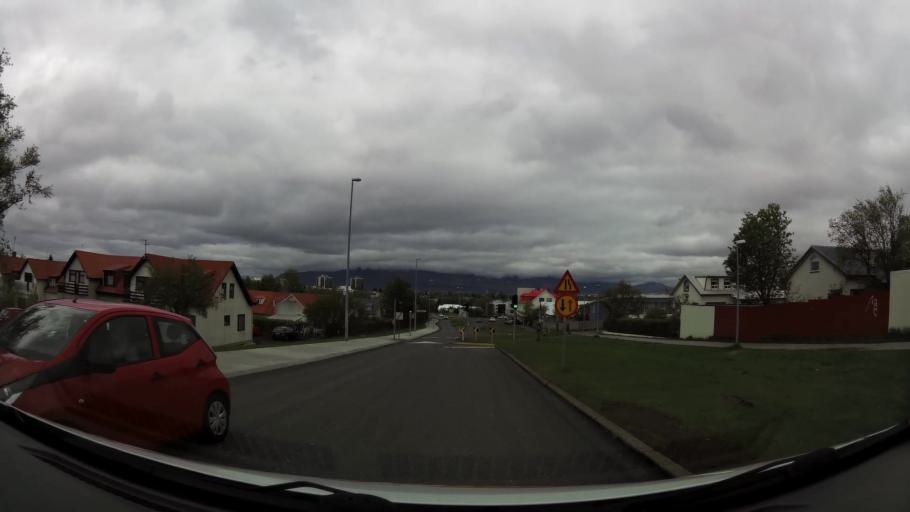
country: IS
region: Capital Region
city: Reykjavik
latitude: 64.1247
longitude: -21.8655
